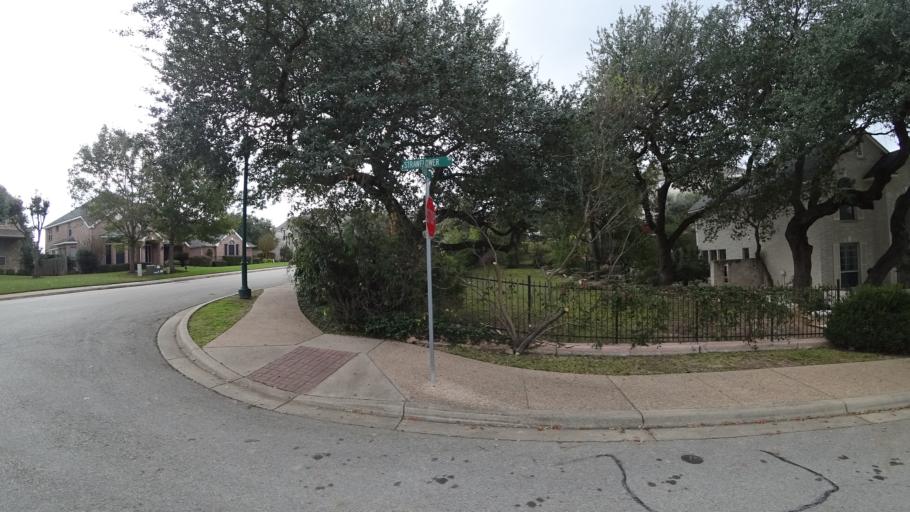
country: US
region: Texas
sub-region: Travis County
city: Barton Creek
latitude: 30.3135
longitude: -97.8971
